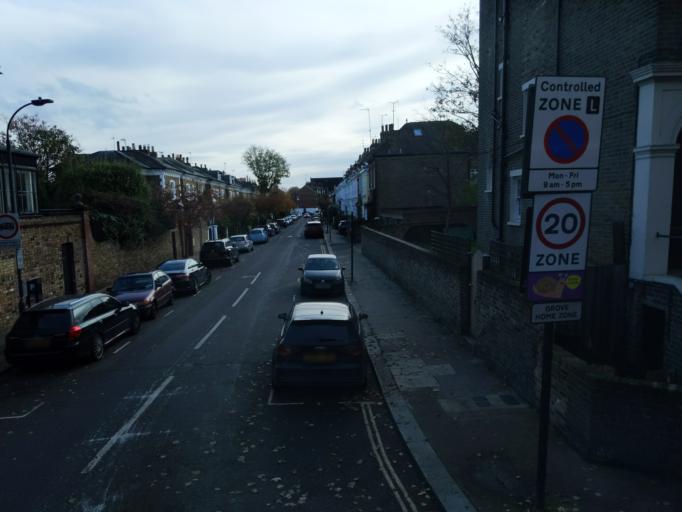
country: GB
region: England
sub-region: Greater London
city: Hammersmith
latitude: 51.5002
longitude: -0.2361
